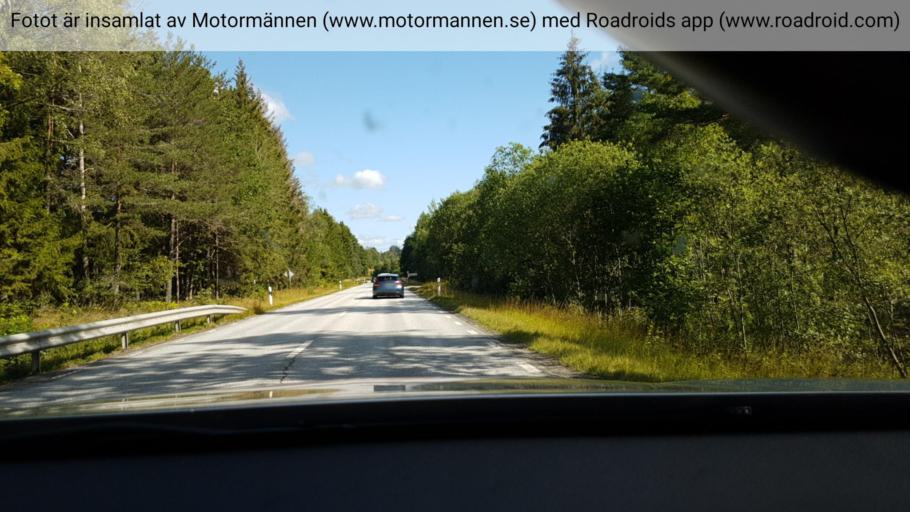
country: SE
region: Stockholm
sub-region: Norrtalje Kommun
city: Norrtalje
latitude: 59.7268
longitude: 18.6789
